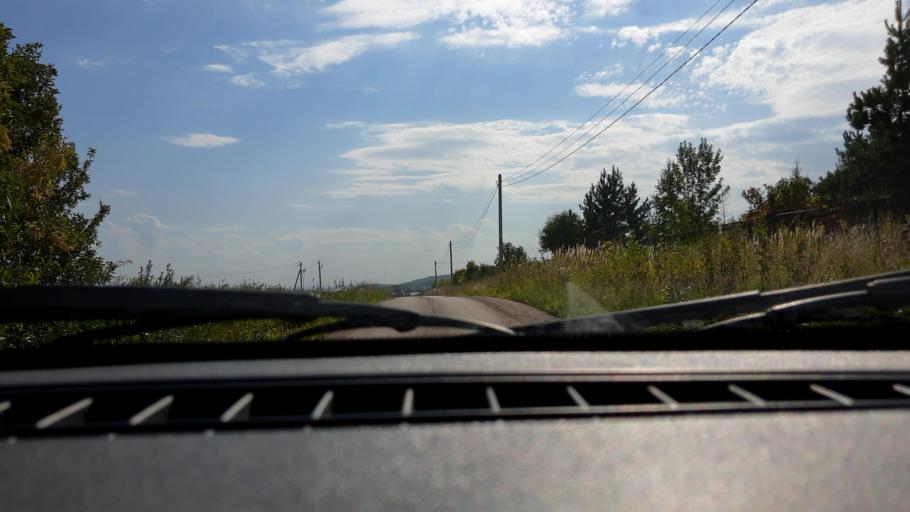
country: RU
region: Bashkortostan
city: Ufa
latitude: 54.8496
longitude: 56.1621
